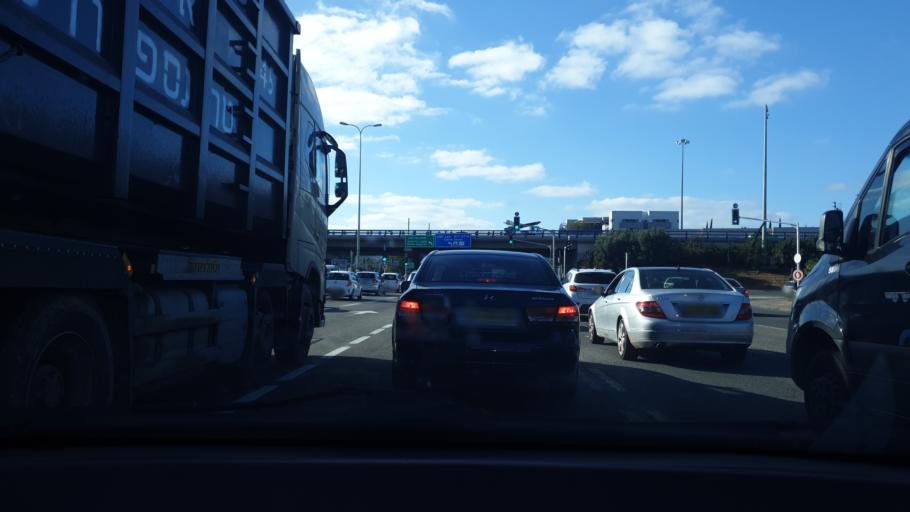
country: IL
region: Tel Aviv
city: Holon
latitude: 32.0378
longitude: 34.7797
